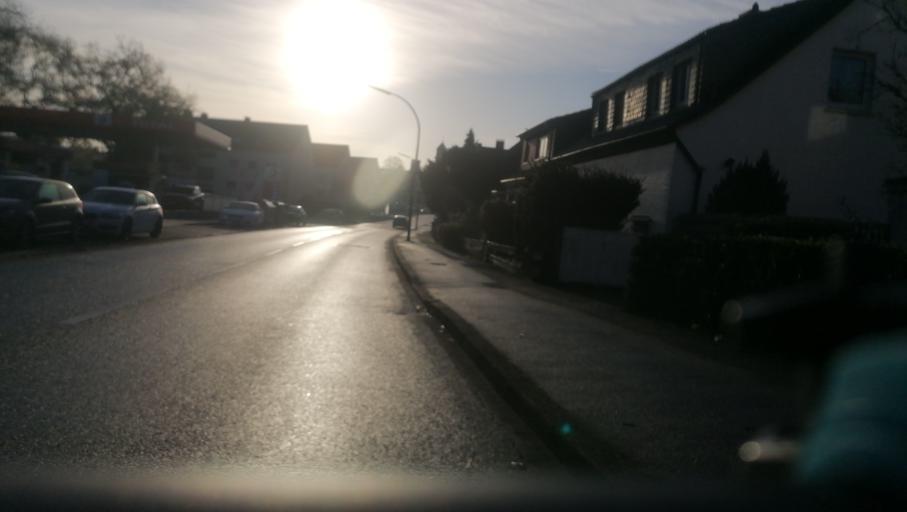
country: DE
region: North Rhine-Westphalia
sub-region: Regierungsbezirk Arnsberg
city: Dortmund
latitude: 51.4684
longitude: 7.4922
